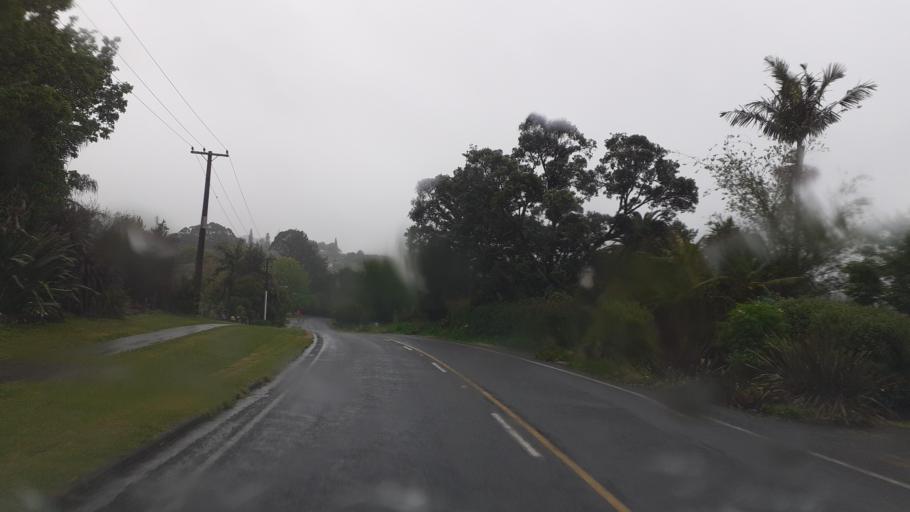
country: NZ
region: Northland
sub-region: Far North District
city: Kerikeri
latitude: -35.2061
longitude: 173.9658
